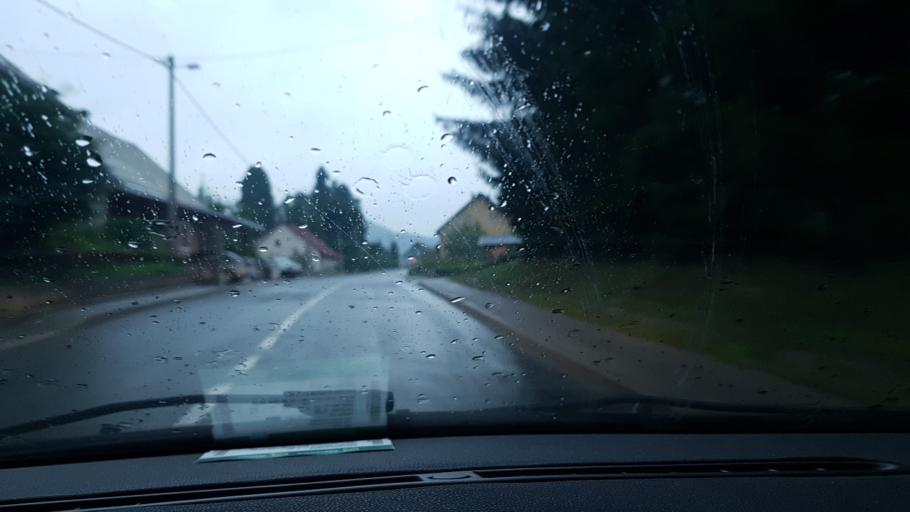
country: HR
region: Primorsko-Goranska
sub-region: Grad Delnice
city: Delnice
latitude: 45.3585
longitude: 14.7319
